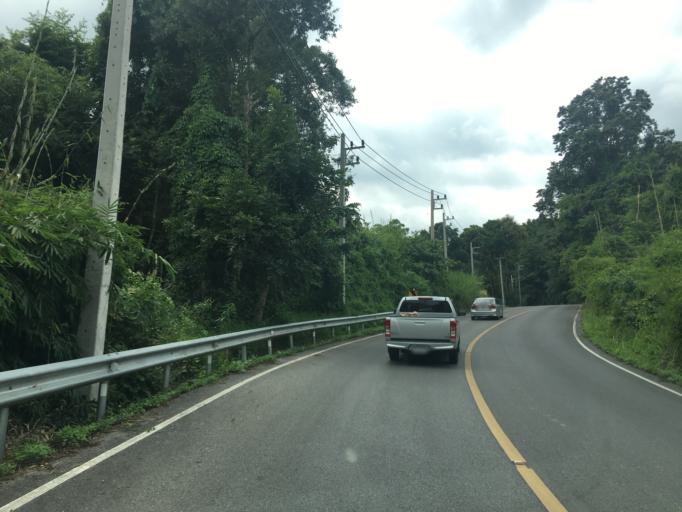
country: TH
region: Nan
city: Ban Luang
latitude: 18.8740
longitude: 100.5295
